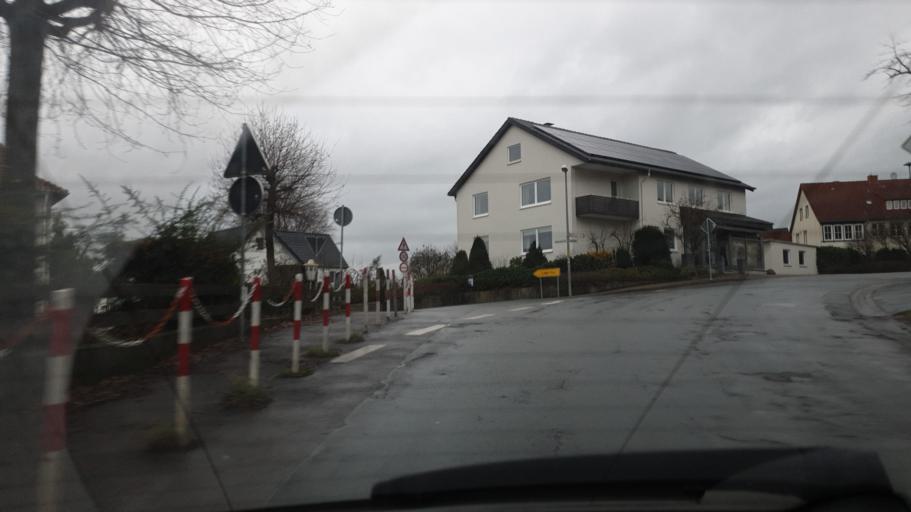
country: DE
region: North Rhine-Westphalia
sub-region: Regierungsbezirk Detmold
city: Detmold
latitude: 51.9799
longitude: 8.8449
